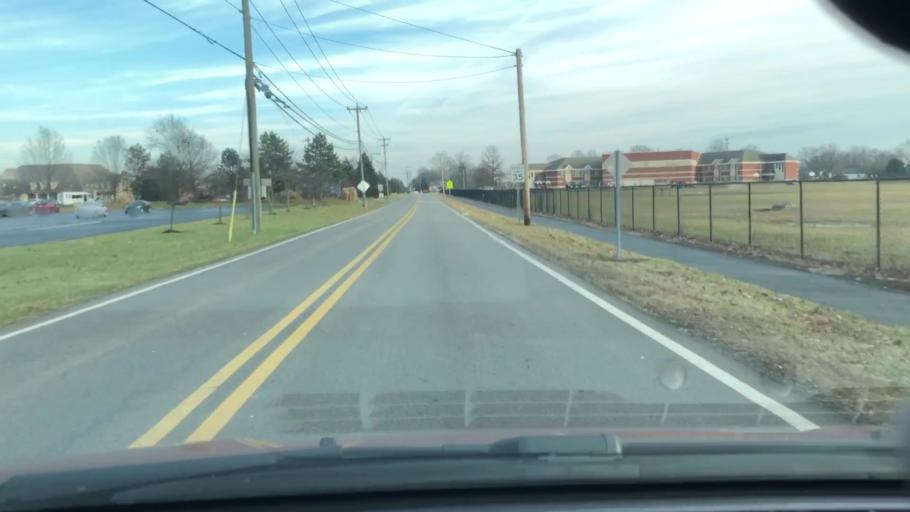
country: US
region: Ohio
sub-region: Franklin County
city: Westerville
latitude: 40.1708
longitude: -82.9147
